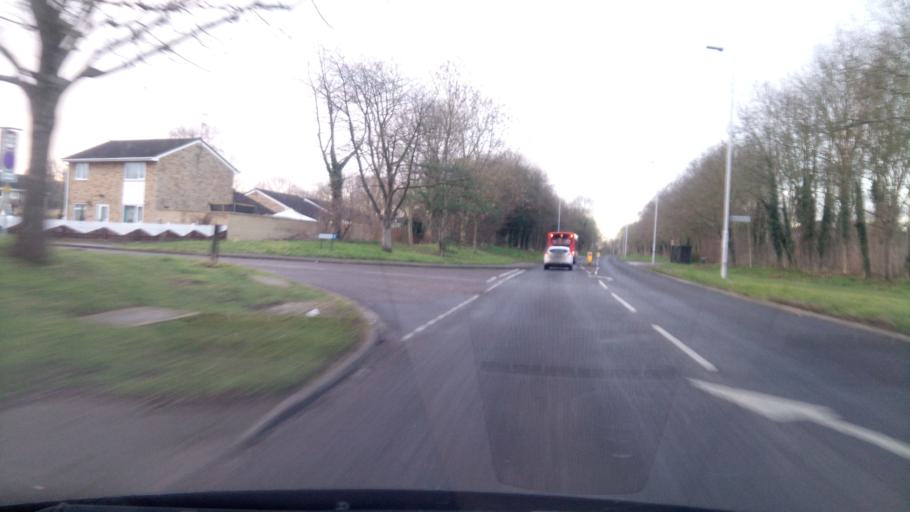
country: GB
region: England
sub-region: Peterborough
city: Marholm
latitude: 52.5862
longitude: -0.2864
